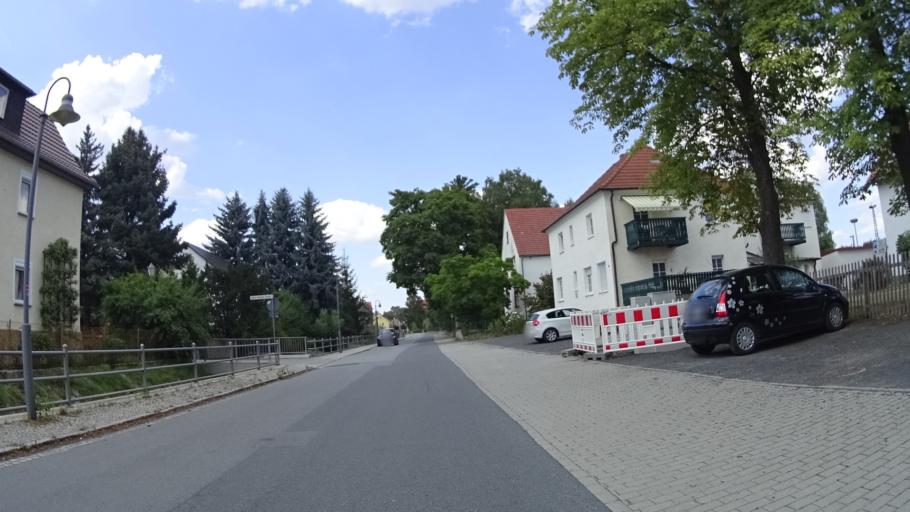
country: DE
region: Saxony
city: Ostritz
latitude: 51.0091
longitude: 14.9324
